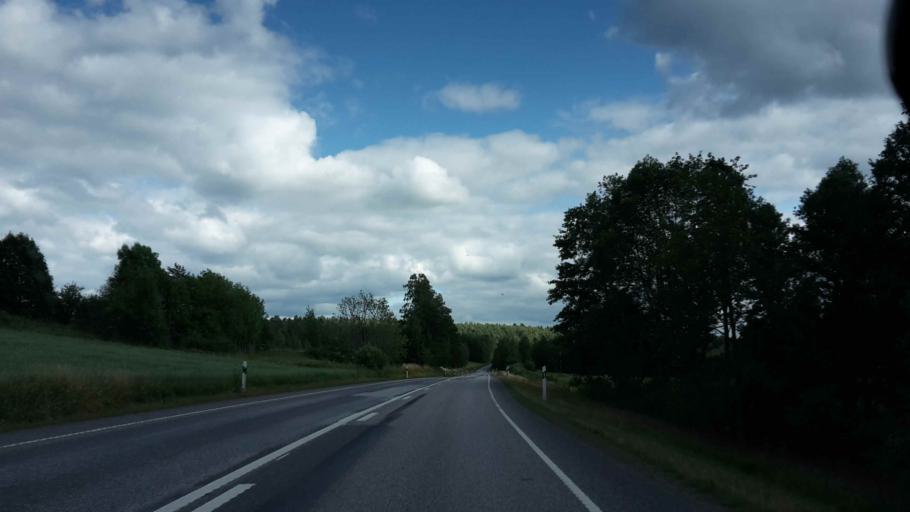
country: SE
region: OEstergoetland
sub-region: Linkopings Kommun
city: Ljungsbro
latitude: 58.7800
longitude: 15.5080
